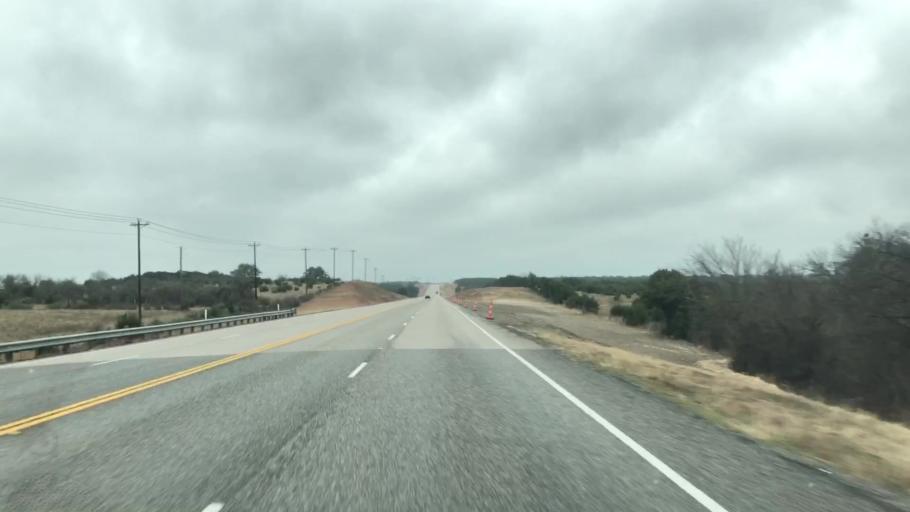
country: US
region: Texas
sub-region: Burnet County
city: Burnet
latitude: 30.9159
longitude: -98.2374
